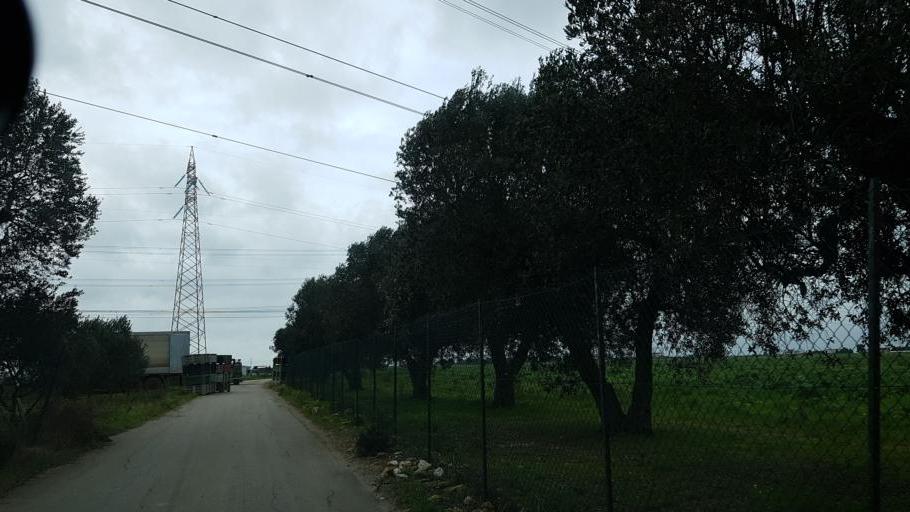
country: IT
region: Apulia
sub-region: Provincia di Brindisi
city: La Rosa
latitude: 40.5999
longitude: 17.9215
